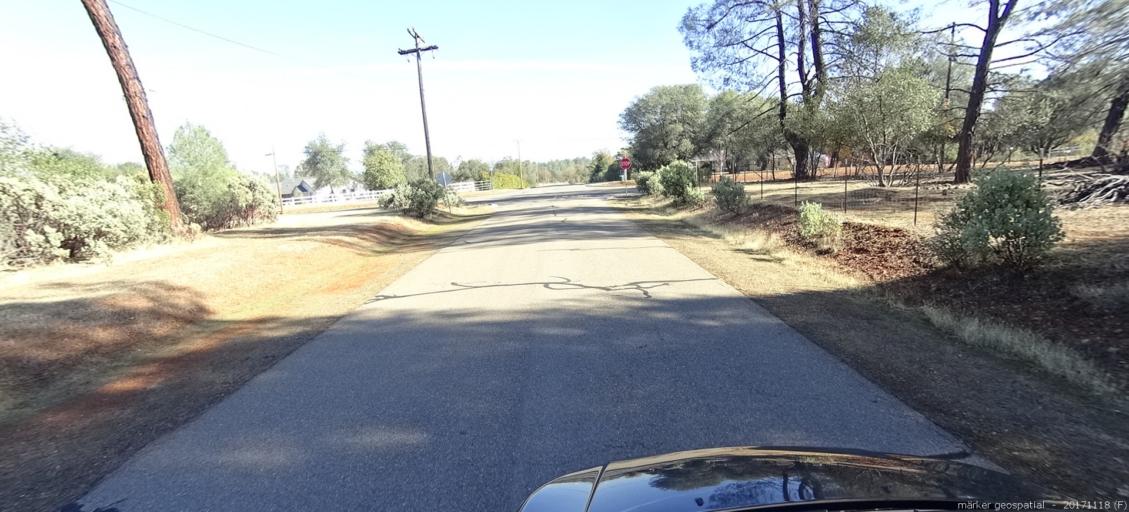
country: US
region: California
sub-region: Shasta County
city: Redding
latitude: 40.4648
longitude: -122.4552
